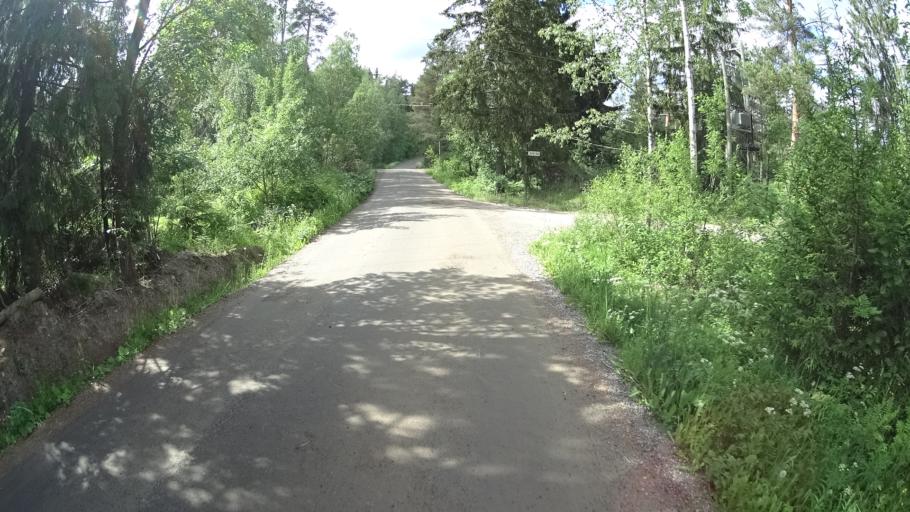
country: FI
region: Uusimaa
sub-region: Helsinki
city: Sibbo
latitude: 60.2869
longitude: 25.3125
